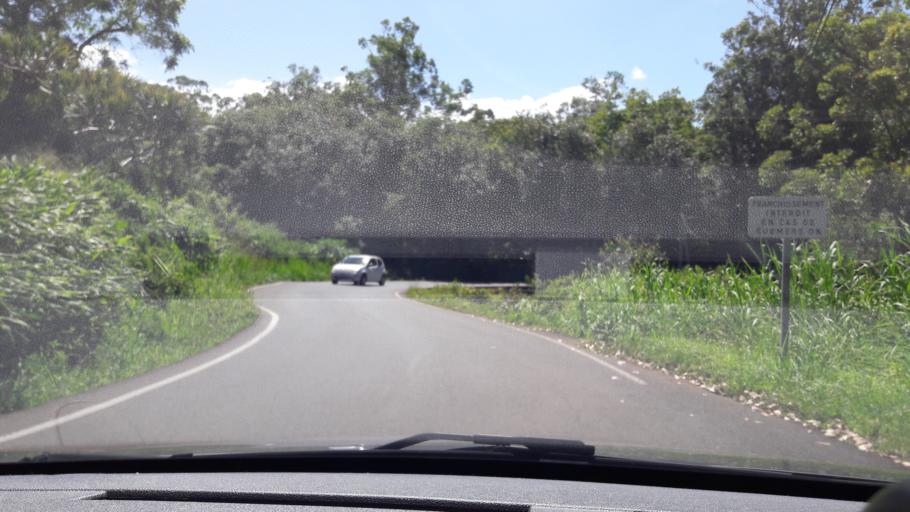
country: RE
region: Reunion
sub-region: Reunion
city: Saint-Benoit
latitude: -21.0866
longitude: 55.6978
